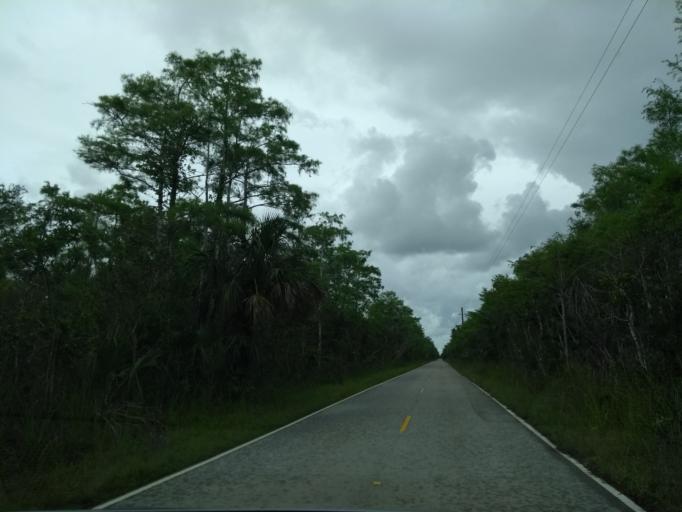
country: US
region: Florida
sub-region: Miami-Dade County
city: The Hammocks
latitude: 25.7613
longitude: -80.9015
